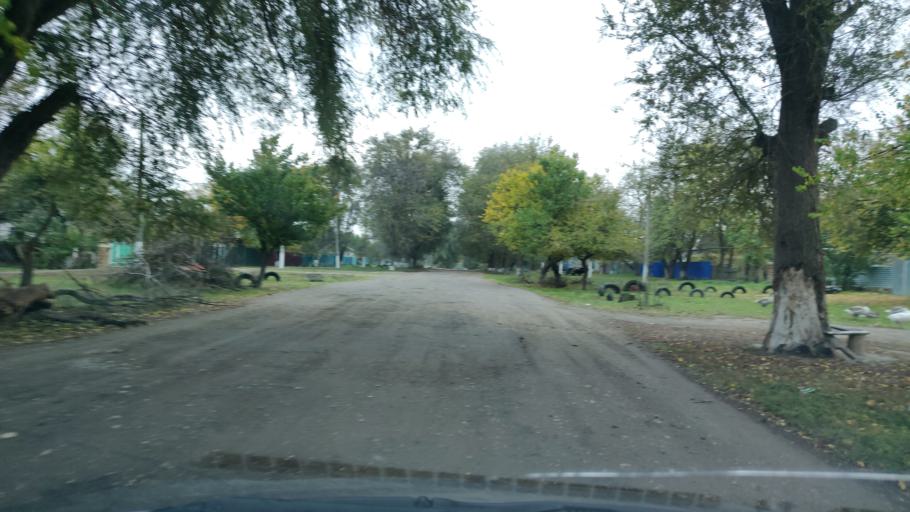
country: RU
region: Stavropol'skiy
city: Irgakly
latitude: 44.2431
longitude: 44.7209
